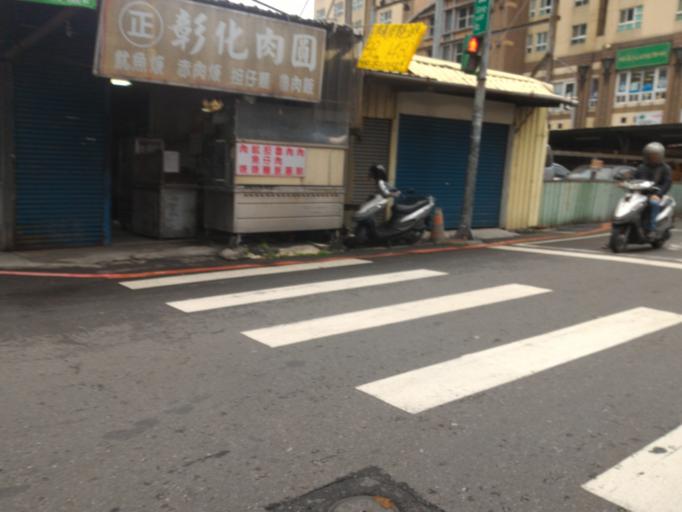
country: TW
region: Taipei
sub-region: Taipei
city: Banqiao
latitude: 25.0407
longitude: 121.4566
